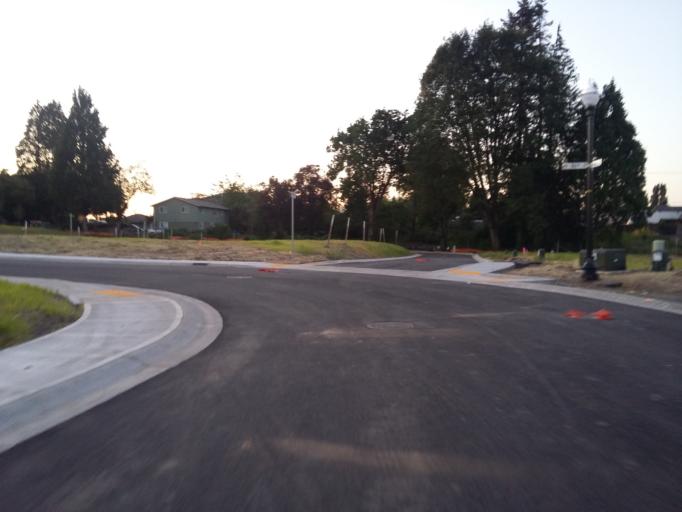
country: US
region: Washington
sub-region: Clark County
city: Hazel Dell
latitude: 45.6842
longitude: -122.6583
